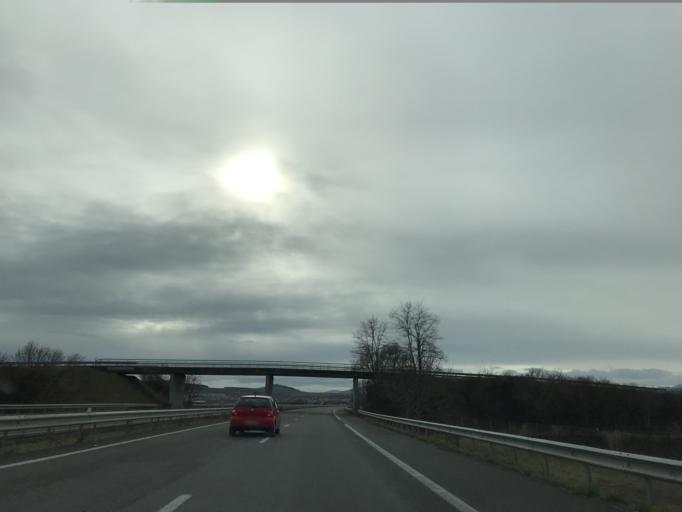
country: FR
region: Auvergne
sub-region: Departement du Puy-de-Dome
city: Malintrat
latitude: 45.8054
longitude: 3.2178
